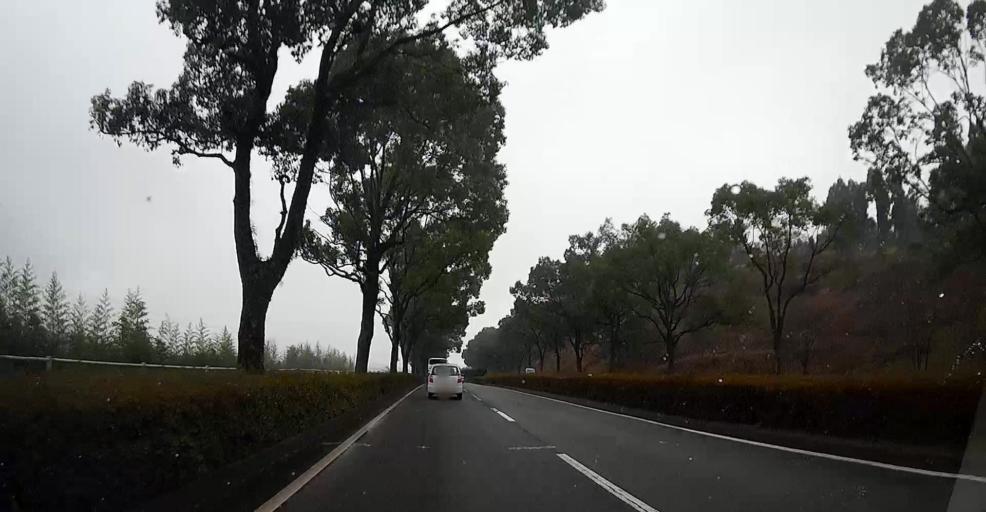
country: JP
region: Kumamoto
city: Ozu
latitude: 32.8179
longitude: 130.8425
